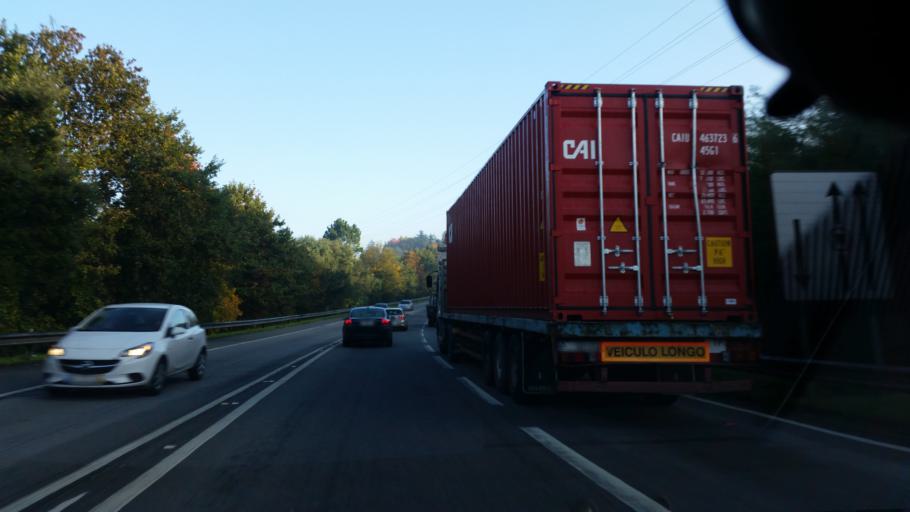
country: PT
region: Porto
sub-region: Santo Tirso
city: Sao Miguel do Couto
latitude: 41.3312
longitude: -8.4705
